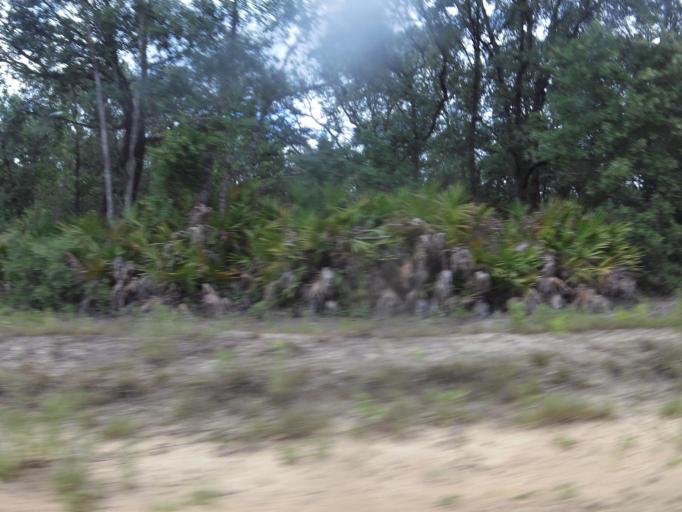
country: US
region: Florida
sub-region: Clay County
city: Green Cove Springs
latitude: 29.9132
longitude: -81.7865
